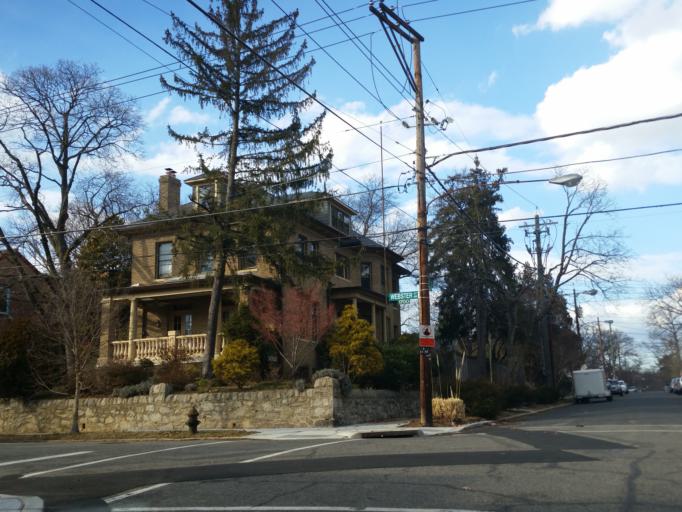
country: US
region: Maryland
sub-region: Montgomery County
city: Takoma Park
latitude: 38.9439
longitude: -77.0388
